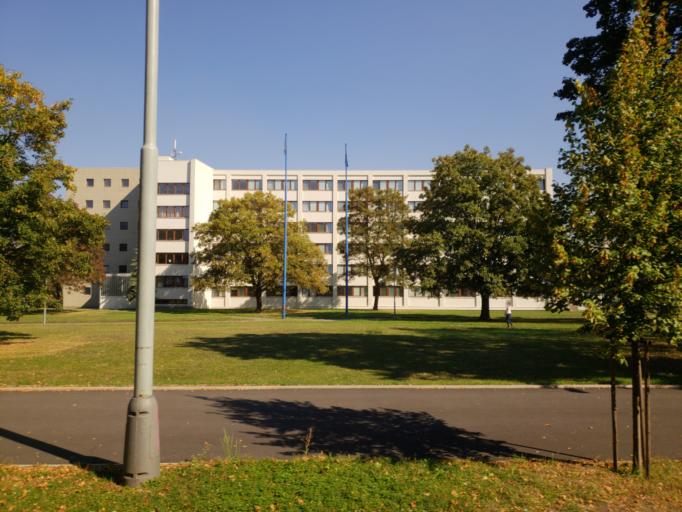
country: CZ
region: Praha
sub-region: Praha 1
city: Mala Strana
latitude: 50.0811
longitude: 14.3899
